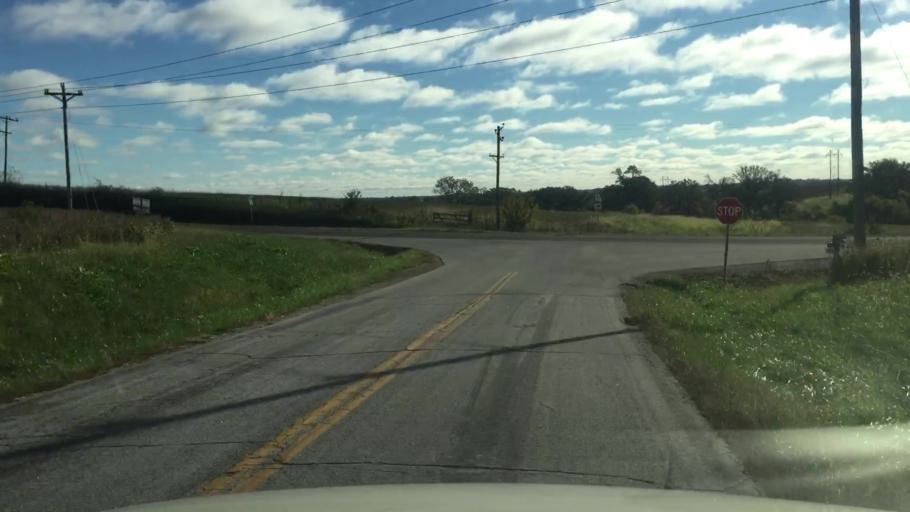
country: US
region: Missouri
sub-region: Howard County
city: Fayette
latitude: 39.1044
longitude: -92.7346
